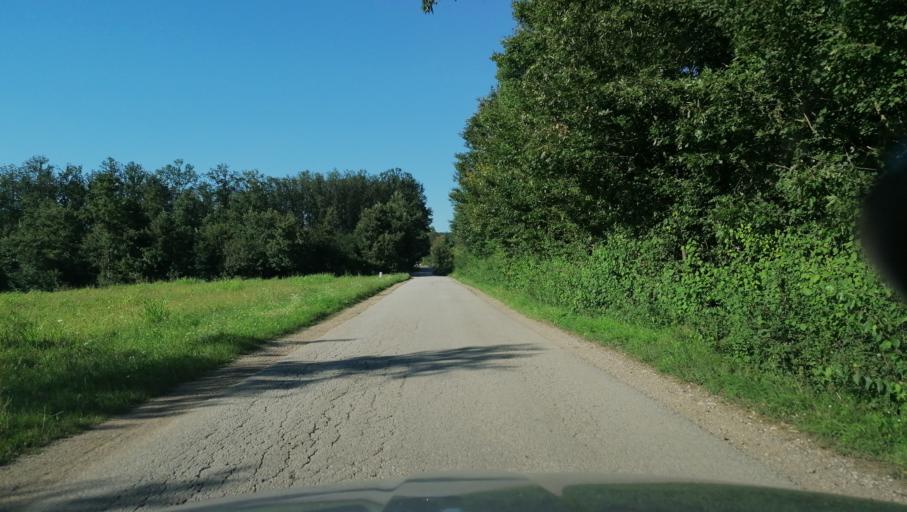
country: RS
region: Central Serbia
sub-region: Sumadijski Okrug
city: Knic
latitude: 43.8829
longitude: 20.6141
